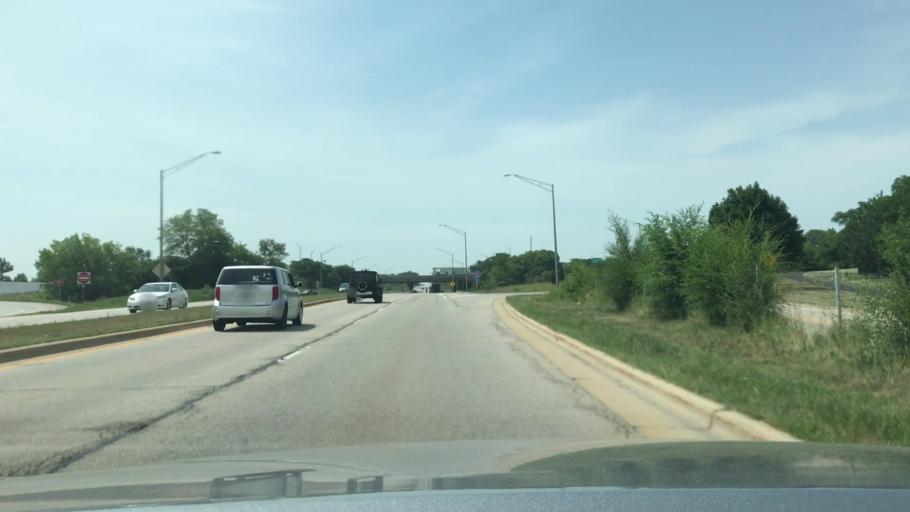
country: US
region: Illinois
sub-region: DuPage County
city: Darien
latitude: 41.7202
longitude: -88.0071
